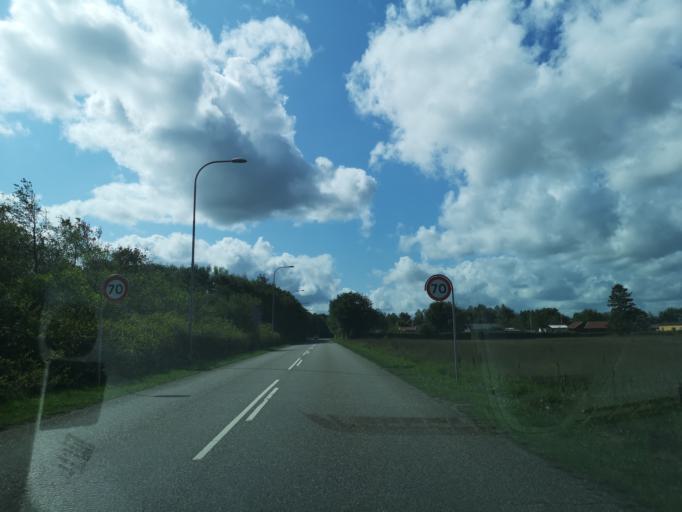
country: DK
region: Central Jutland
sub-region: Holstebro Kommune
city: Holstebro
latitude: 56.3825
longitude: 8.5755
